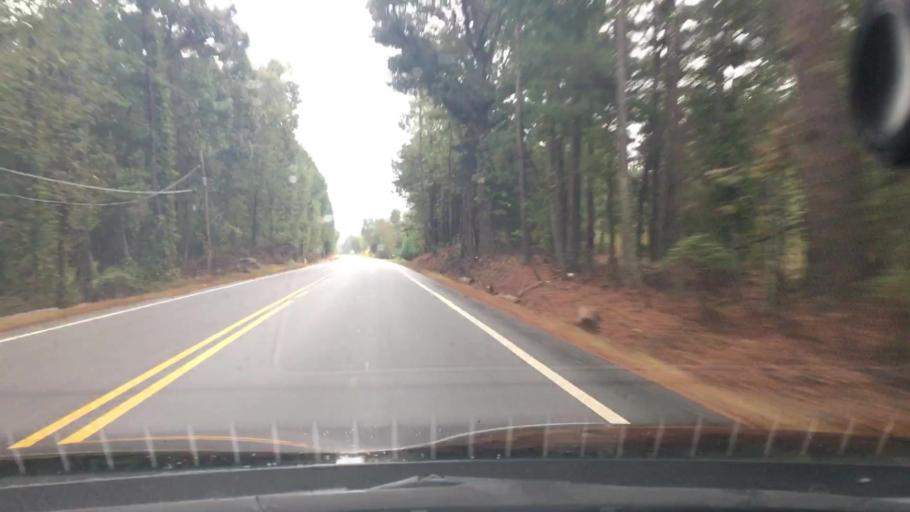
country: US
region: Georgia
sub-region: Spalding County
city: Experiment
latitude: 33.2408
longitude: -84.3543
